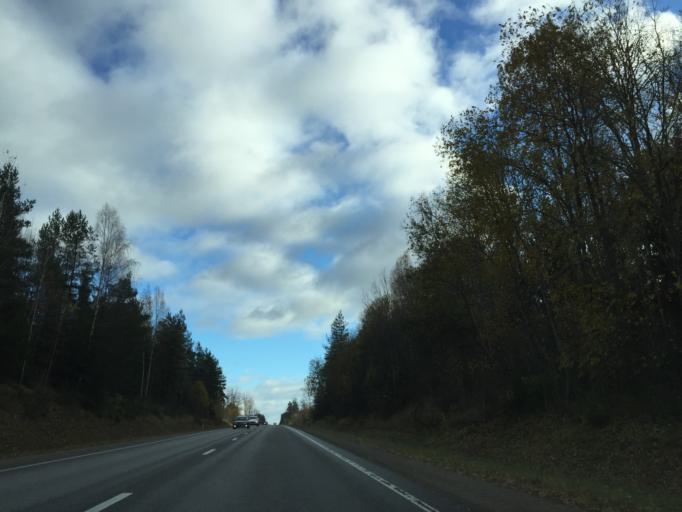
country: LV
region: Tukuma Rajons
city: Tukums
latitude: 56.9925
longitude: 23.0203
